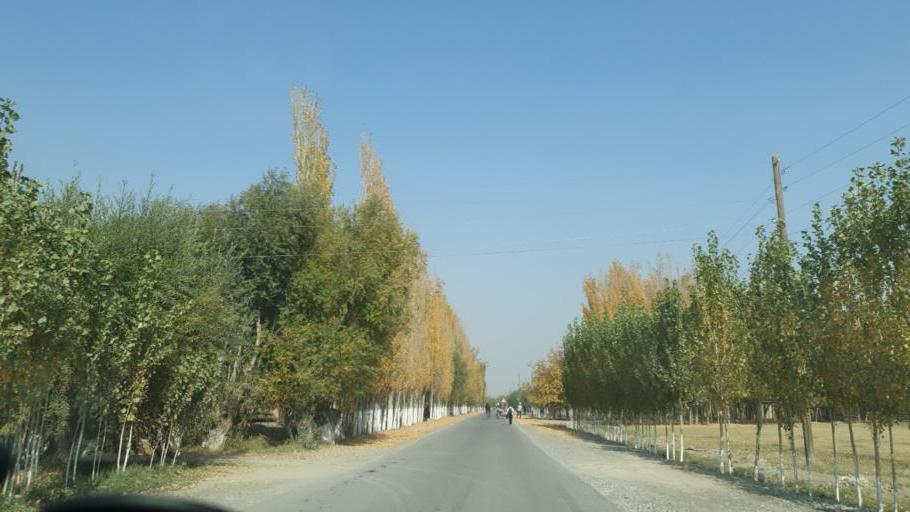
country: UZ
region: Fergana
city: Beshariq
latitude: 40.4906
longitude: 70.6207
